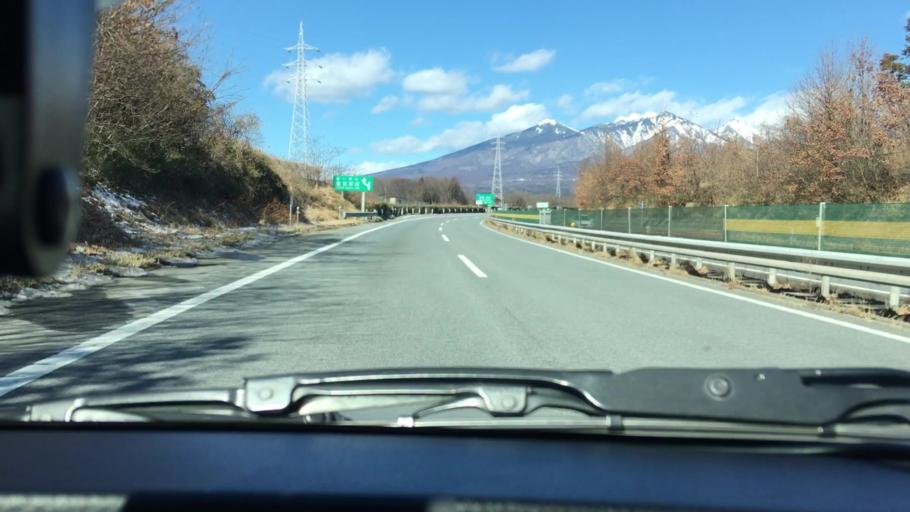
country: JP
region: Yamanashi
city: Nirasaki
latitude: 35.8251
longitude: 138.3933
